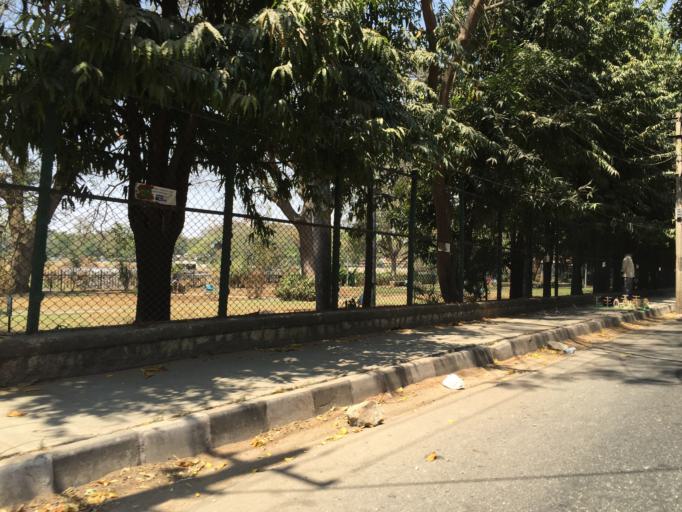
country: IN
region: Karnataka
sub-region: Bangalore Urban
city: Bangalore
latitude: 12.9852
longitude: 77.6224
